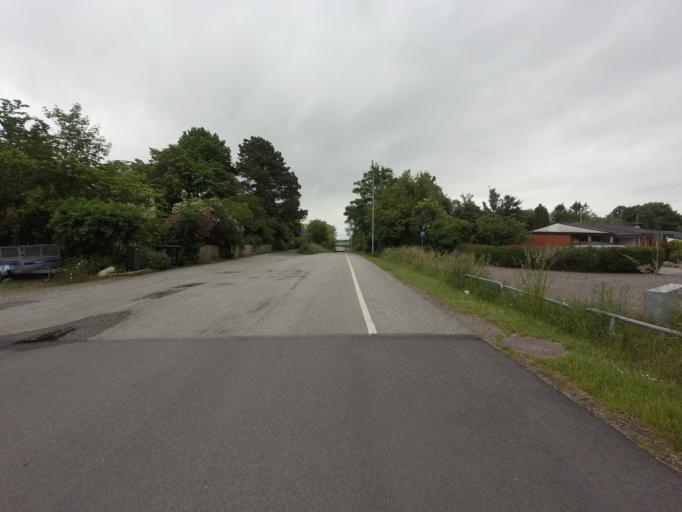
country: SE
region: Skane
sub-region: Staffanstorps Kommun
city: Hjaerup
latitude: 55.6486
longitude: 13.1161
